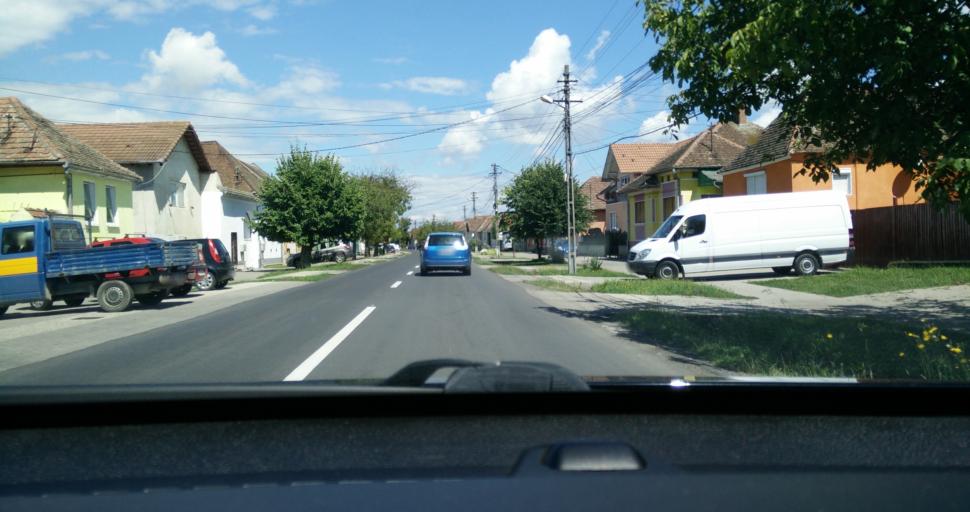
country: RO
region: Alba
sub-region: Municipiul Sebes
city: Petresti
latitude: 45.9217
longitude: 23.5620
